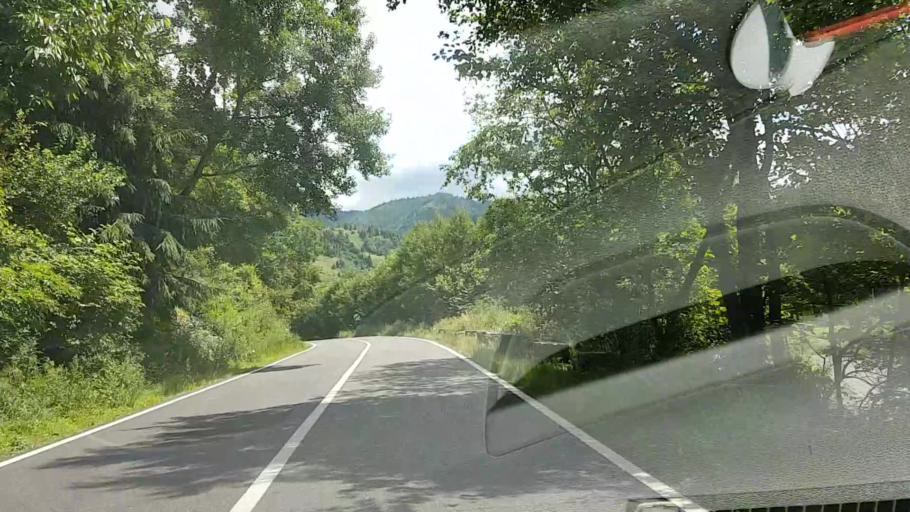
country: RO
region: Suceava
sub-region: Comuna Crucea
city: Crucea
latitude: 47.3937
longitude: 25.5679
